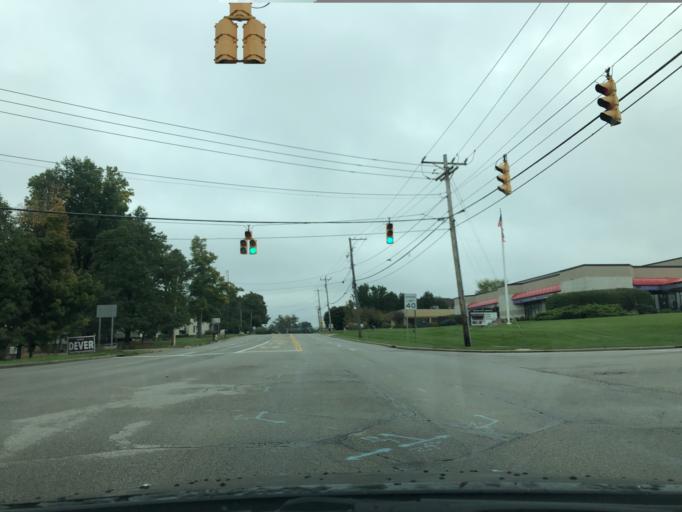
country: US
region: Ohio
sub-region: Hamilton County
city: Highpoint
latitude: 39.2813
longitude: -84.3609
